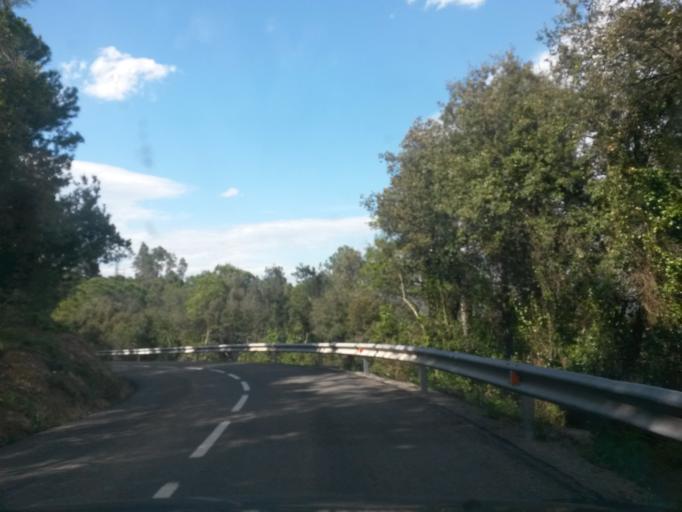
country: ES
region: Catalonia
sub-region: Provincia de Girona
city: Brunyola
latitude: 41.9011
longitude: 2.6815
